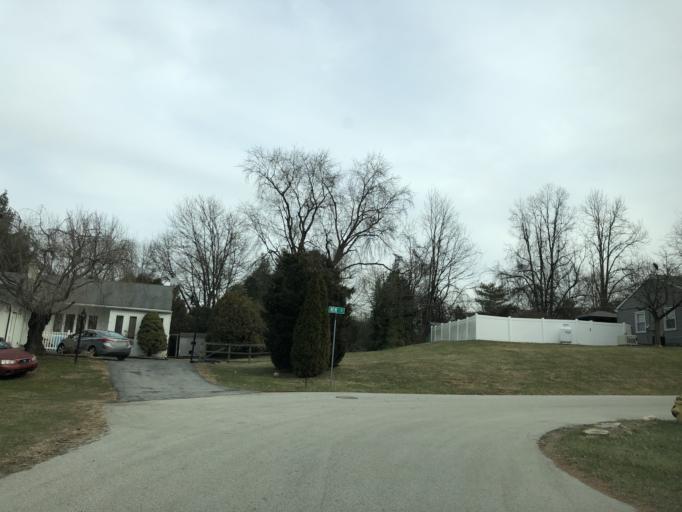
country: US
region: Pennsylvania
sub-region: Chester County
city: Exton
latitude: 40.0268
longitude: -75.6238
